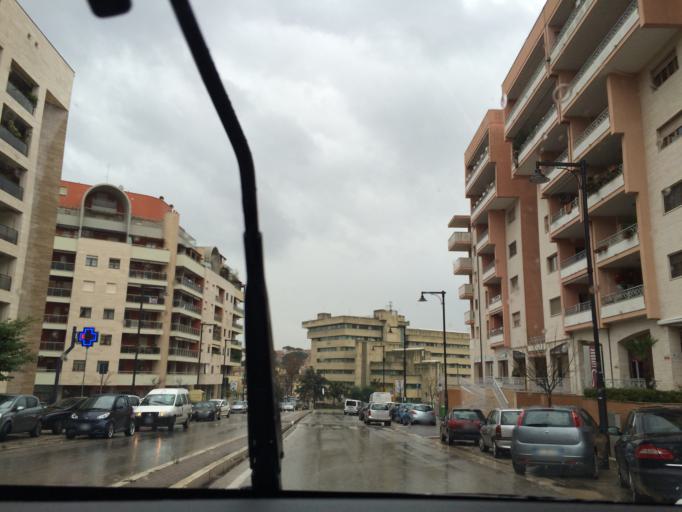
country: IT
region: Basilicate
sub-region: Provincia di Matera
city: Matera
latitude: 40.6684
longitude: 16.5997
